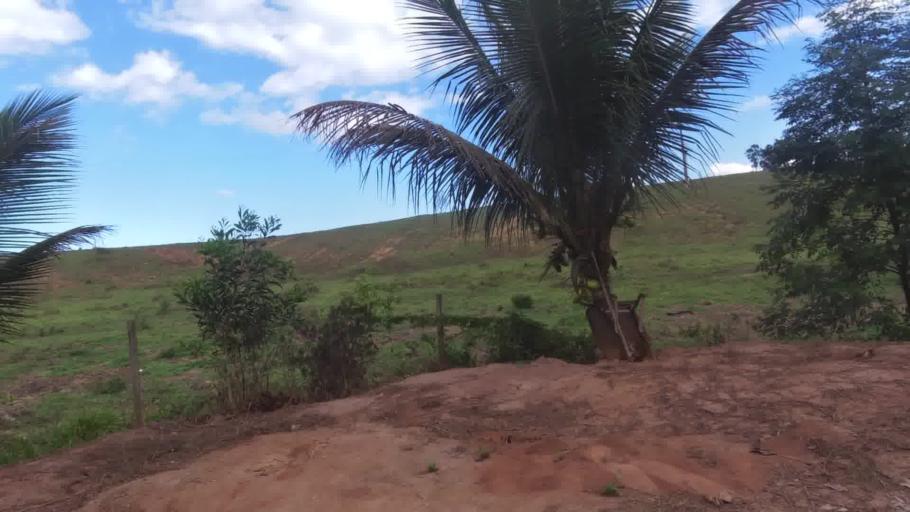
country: BR
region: Espirito Santo
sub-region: Marataizes
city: Marataizes
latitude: -21.1051
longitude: -41.0425
